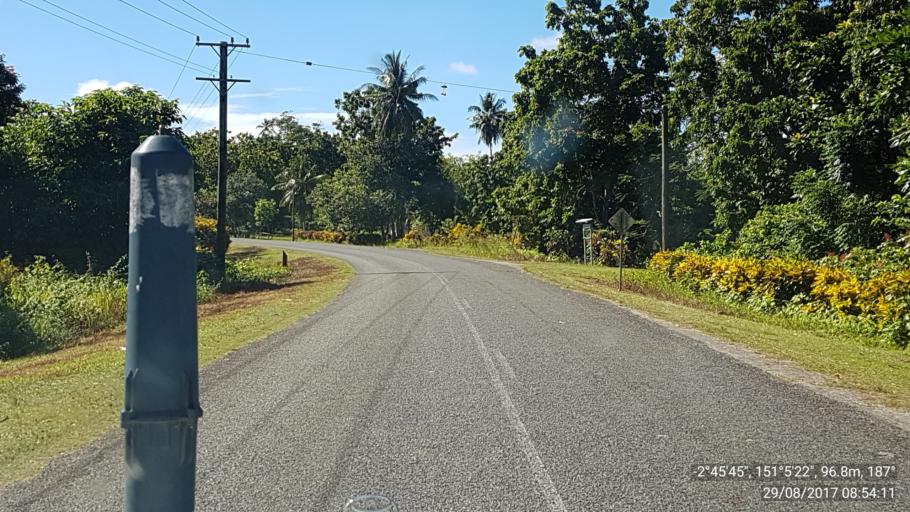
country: PG
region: New Ireland
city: Kavieng
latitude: -2.7625
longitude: 151.0894
